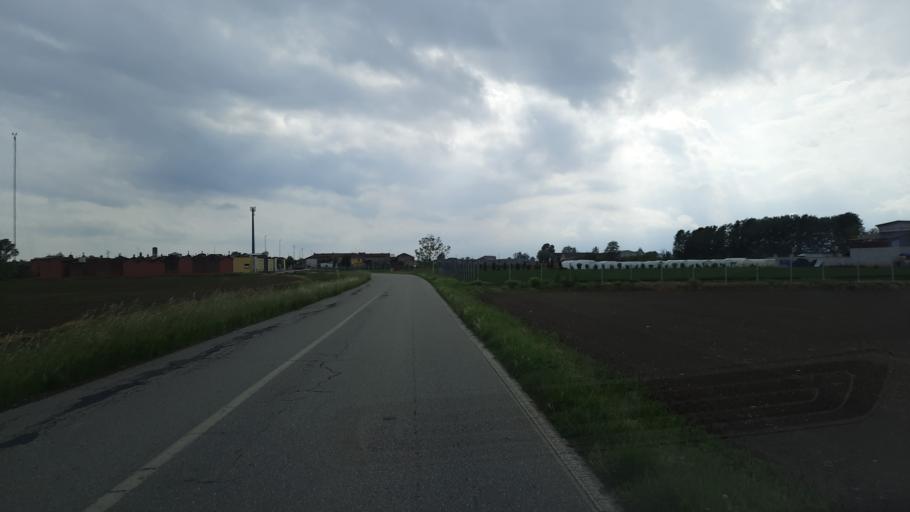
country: IT
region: Lombardy
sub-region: Provincia di Pavia
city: Castelnovetto
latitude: 45.2590
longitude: 8.6207
